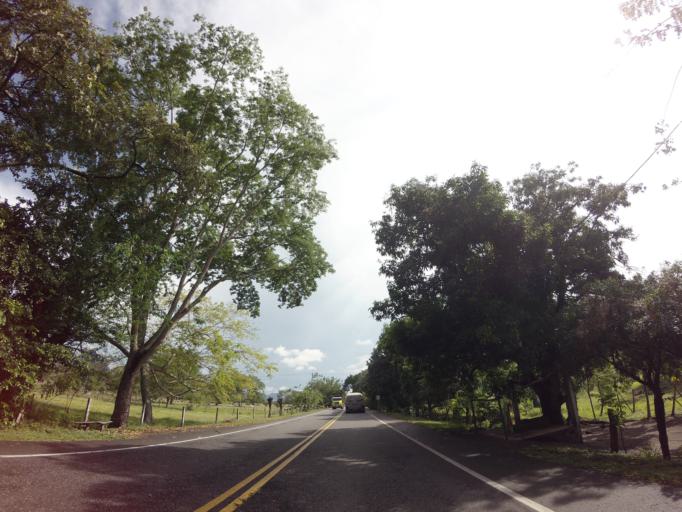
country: CO
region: Tolima
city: Honda
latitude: 5.3211
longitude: -74.7394
